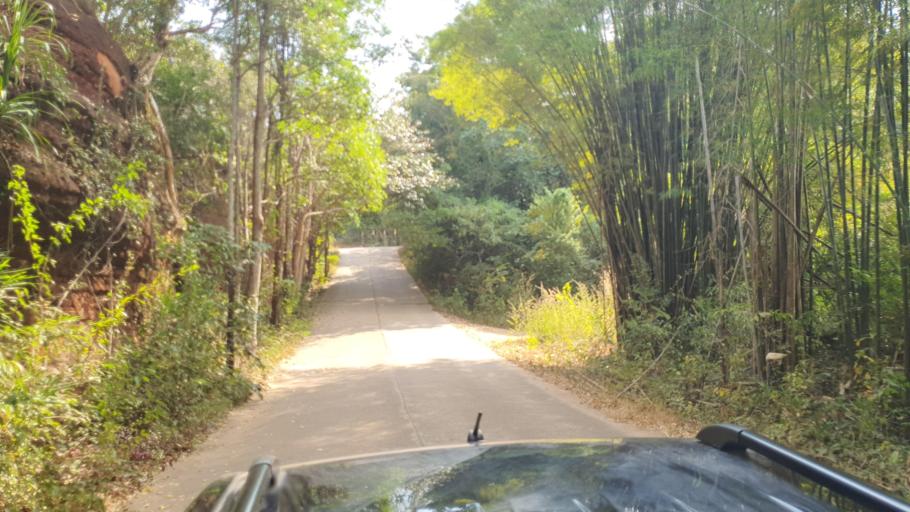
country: TH
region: Changwat Bueng Kan
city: Si Wilai
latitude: 18.2733
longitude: 103.7965
